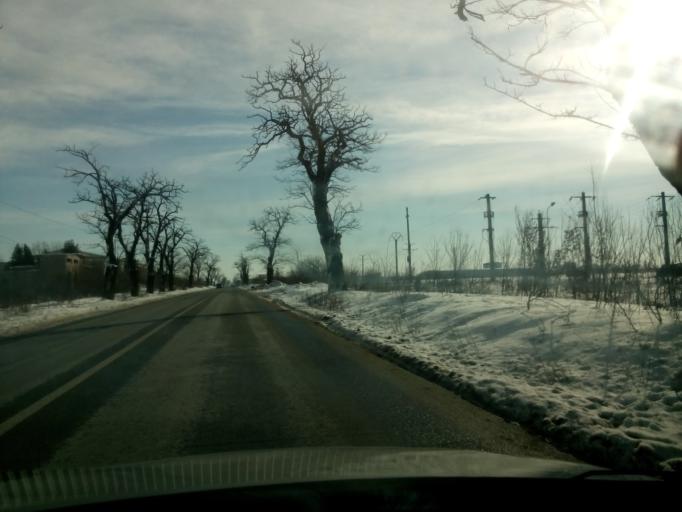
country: RO
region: Ilfov
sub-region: Comuna Popesti-Leordeni
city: Popesti-Leordeni
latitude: 44.3634
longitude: 26.1937
